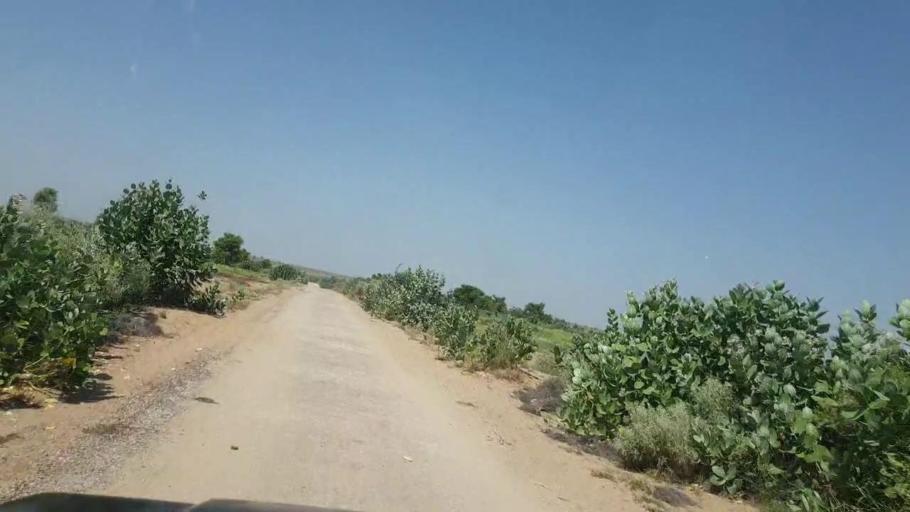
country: PK
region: Sindh
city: Chor
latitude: 25.3645
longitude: 70.3244
